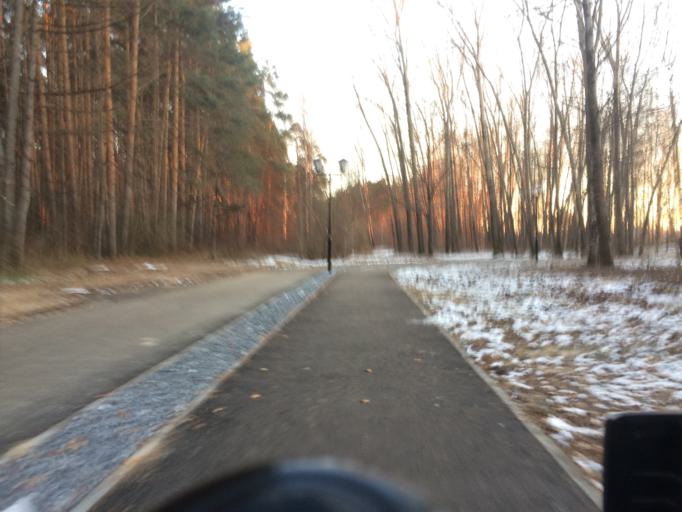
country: RU
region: Mariy-El
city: Yoshkar-Ola
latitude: 56.6237
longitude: 47.9173
